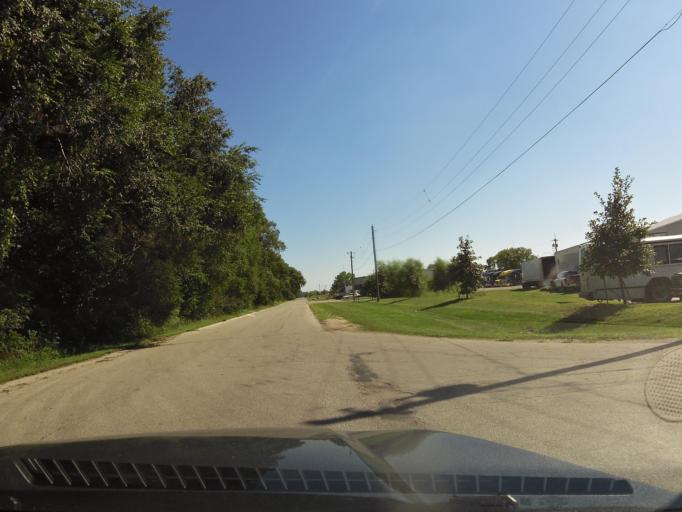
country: US
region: Iowa
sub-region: Black Hawk County
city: Waterloo
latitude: 42.4713
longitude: -92.3182
